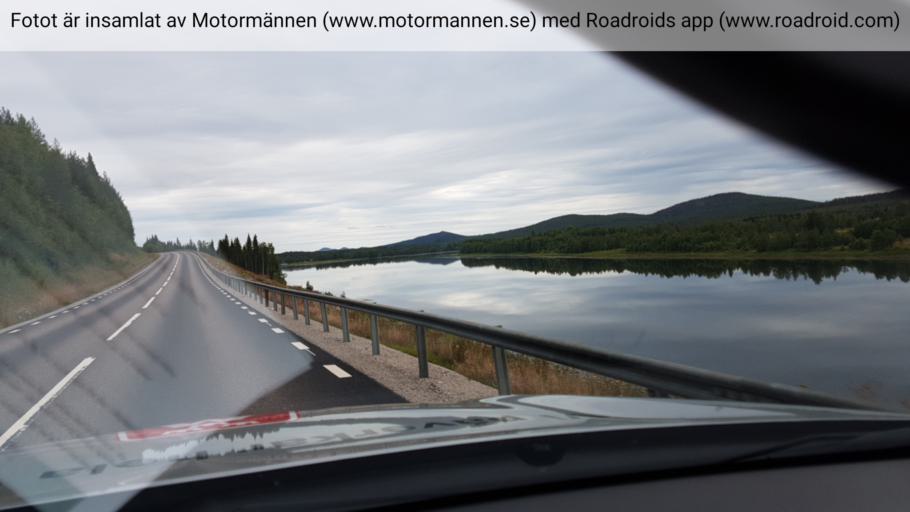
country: SE
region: Norrbotten
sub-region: Overkalix Kommun
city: OEverkalix
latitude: 66.4815
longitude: 22.7857
